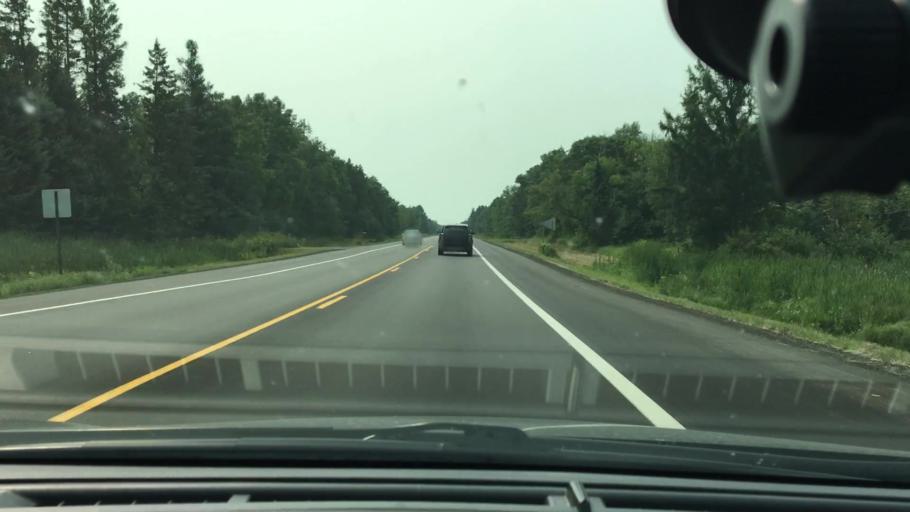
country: US
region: Minnesota
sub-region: Crow Wing County
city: Brainerd
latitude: 46.4548
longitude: -94.1723
